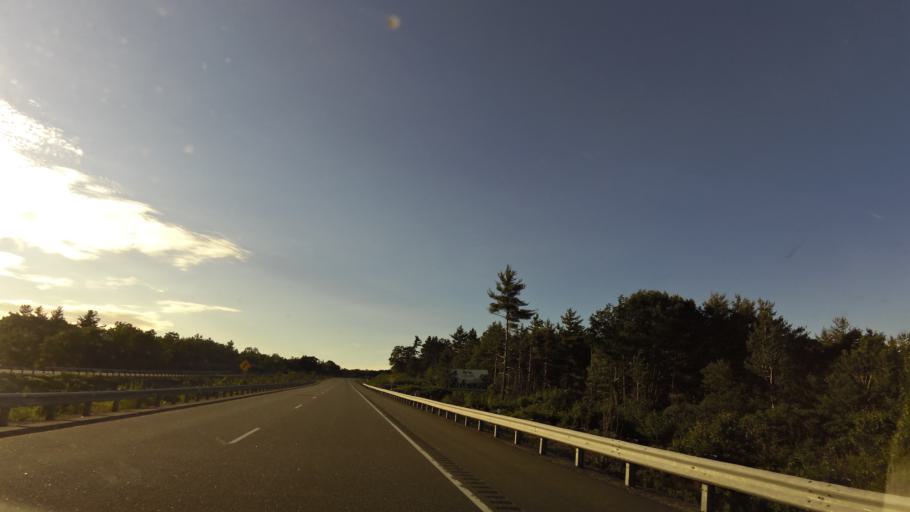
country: CA
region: Ontario
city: Midland
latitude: 44.8678
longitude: -79.7462
